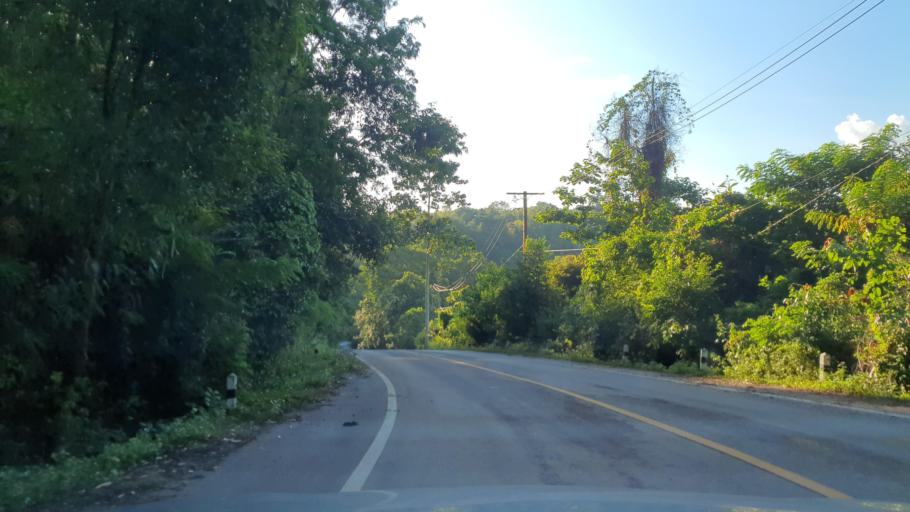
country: TH
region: Chiang Mai
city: Mae On
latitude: 18.8182
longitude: 99.3042
